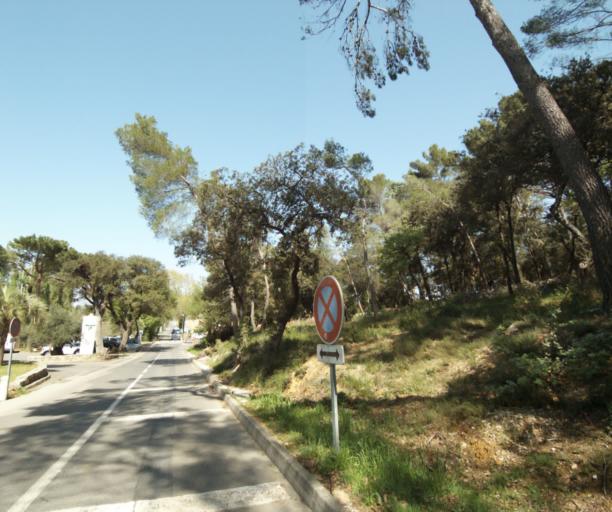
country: FR
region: Languedoc-Roussillon
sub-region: Departement de l'Herault
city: Clapiers
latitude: 43.6518
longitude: 3.8958
